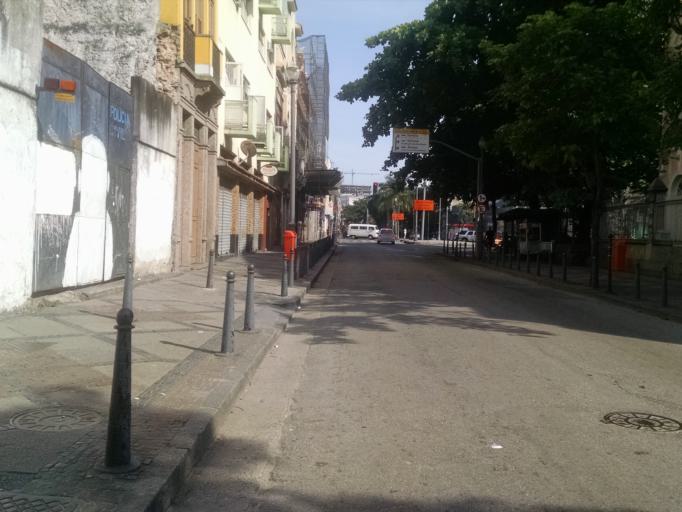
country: BR
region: Rio de Janeiro
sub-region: Rio De Janeiro
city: Rio de Janeiro
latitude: -22.9107
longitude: -43.1827
